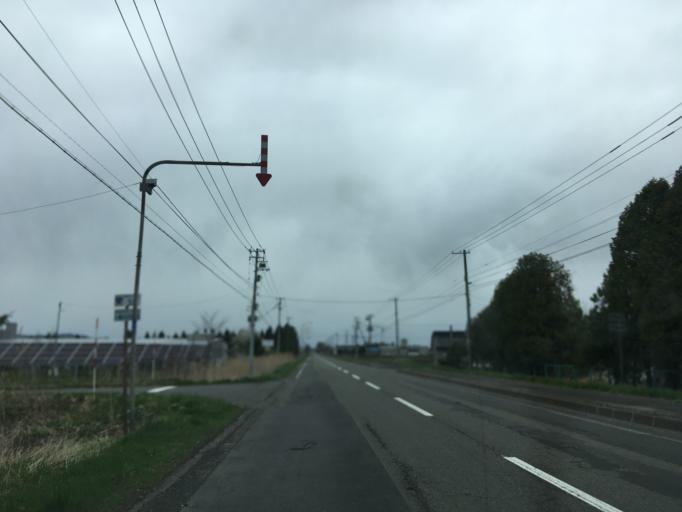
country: JP
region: Hokkaido
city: Chitose
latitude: 42.9319
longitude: 141.8066
